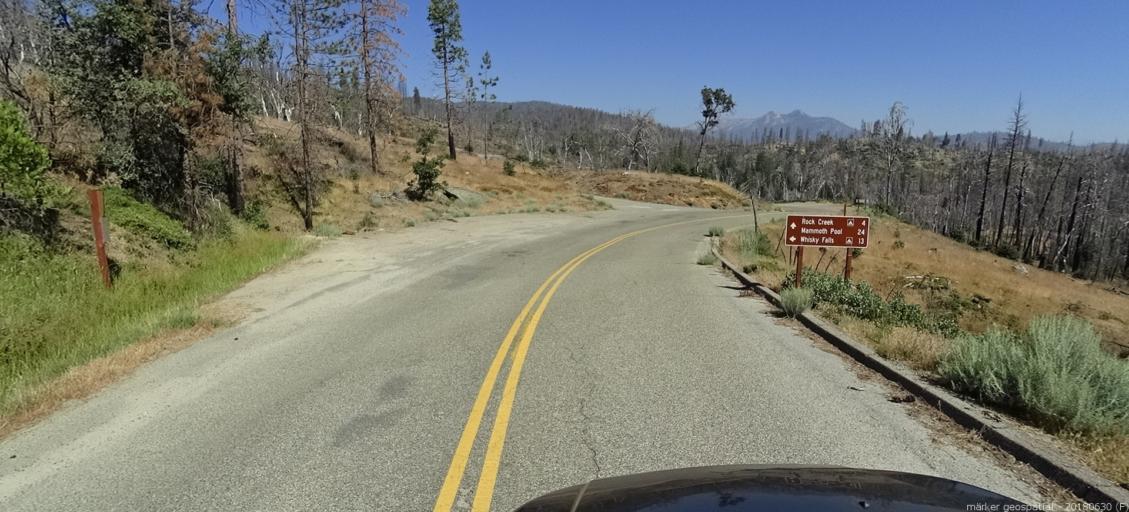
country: US
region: California
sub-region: Fresno County
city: Auberry
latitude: 37.2553
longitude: -119.3513
